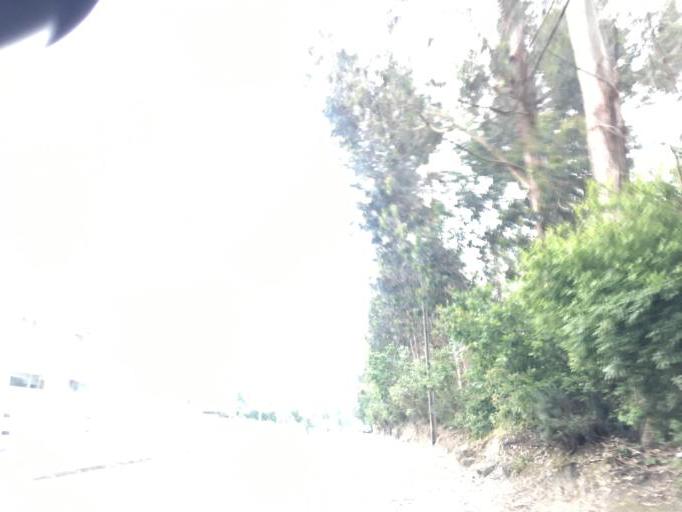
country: PT
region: Porto
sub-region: Maia
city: Nogueira
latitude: 41.2485
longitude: -8.5961
